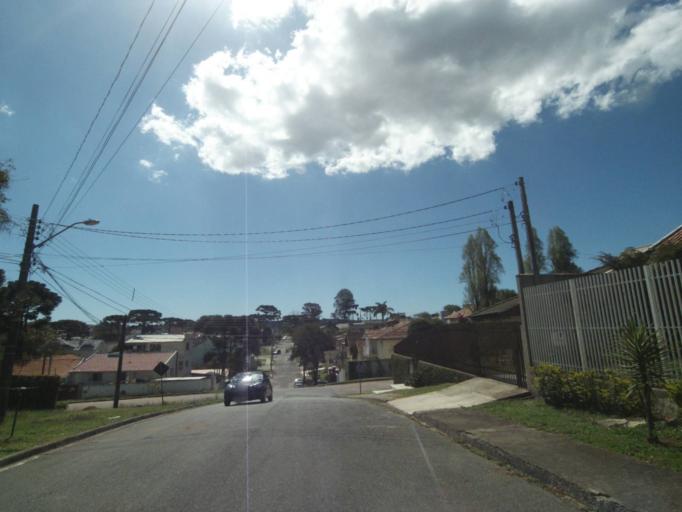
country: BR
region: Parana
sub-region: Curitiba
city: Curitiba
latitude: -25.3811
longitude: -49.2424
